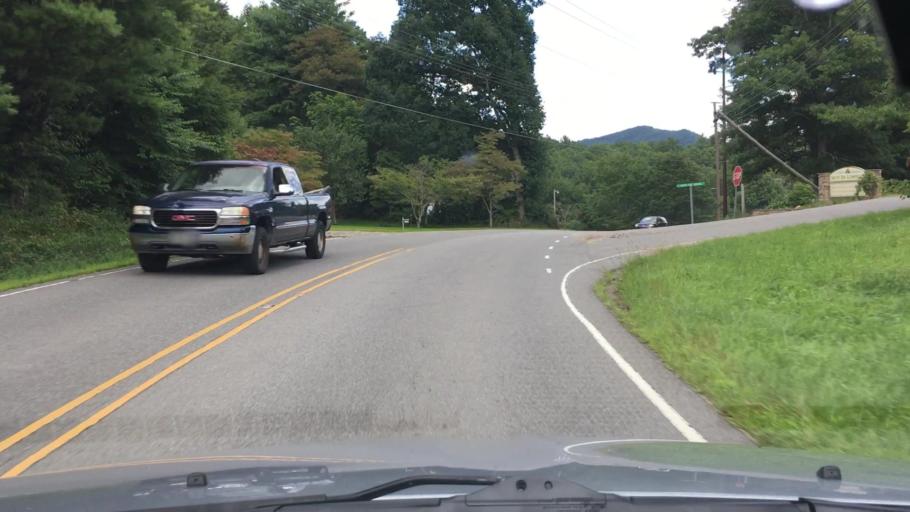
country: US
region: North Carolina
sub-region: Yancey County
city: Burnsville
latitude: 35.8381
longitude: -82.1894
